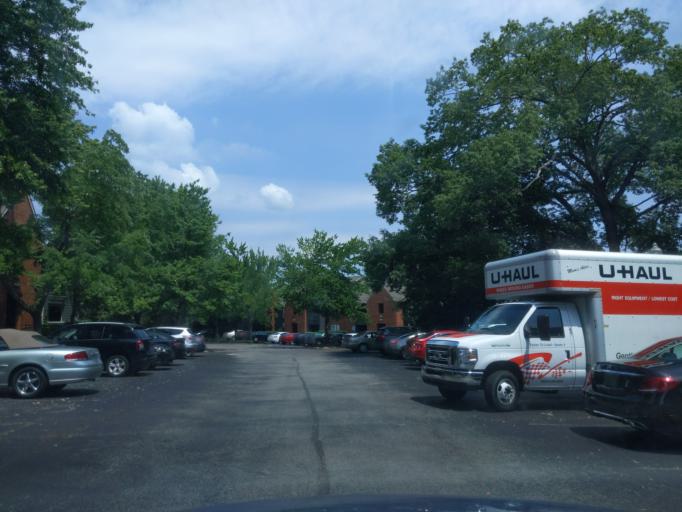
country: US
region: Tennessee
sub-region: Williamson County
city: Brentwood Estates
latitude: 36.0434
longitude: -86.7398
